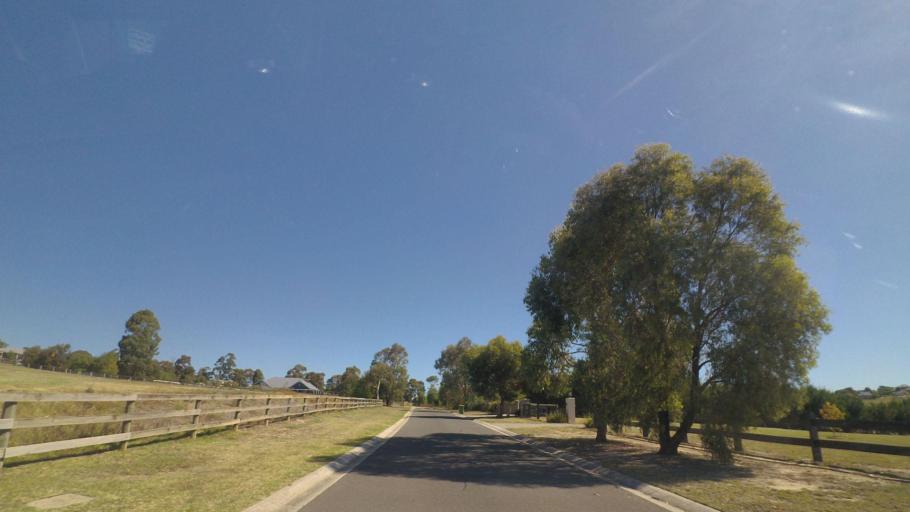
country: AU
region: Victoria
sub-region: Yarra Ranges
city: Chirnside Park
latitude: -37.7473
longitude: 145.3131
